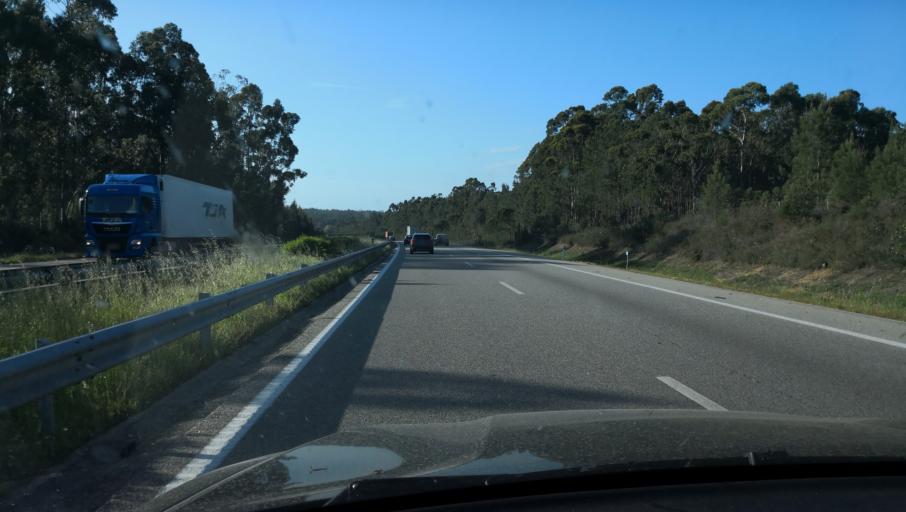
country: PT
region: Aveiro
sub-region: Oliveira do Bairro
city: Oliveira do Bairro
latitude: 40.4856
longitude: -8.5234
